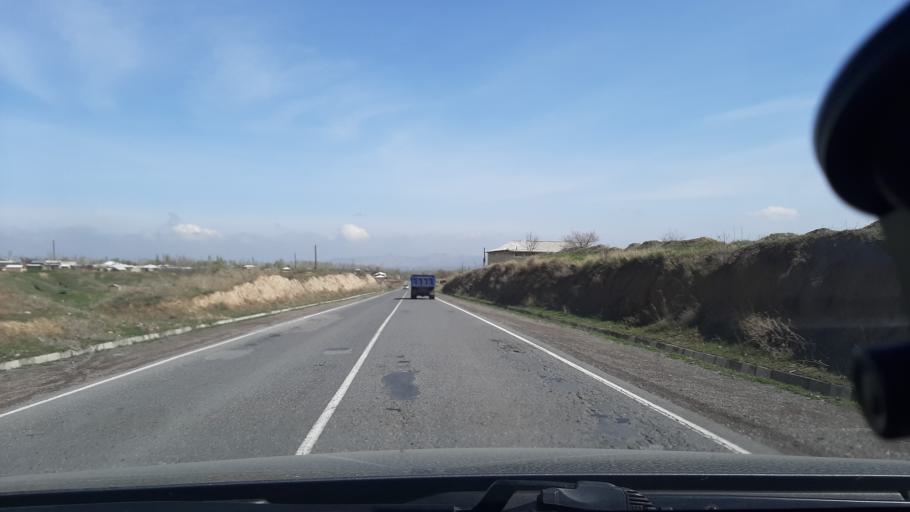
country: TJ
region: Viloyati Sughd
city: Shahriston
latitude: 39.7697
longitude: 68.8230
